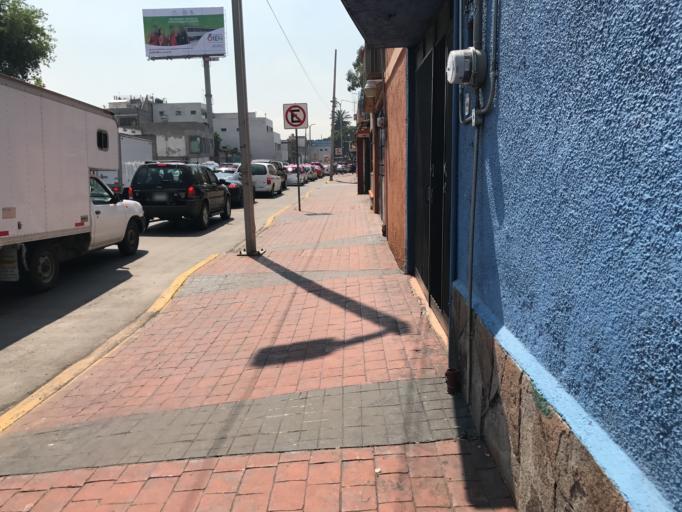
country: MX
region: Mexico
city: Colonia Lindavista
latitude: 19.4795
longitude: -99.1228
